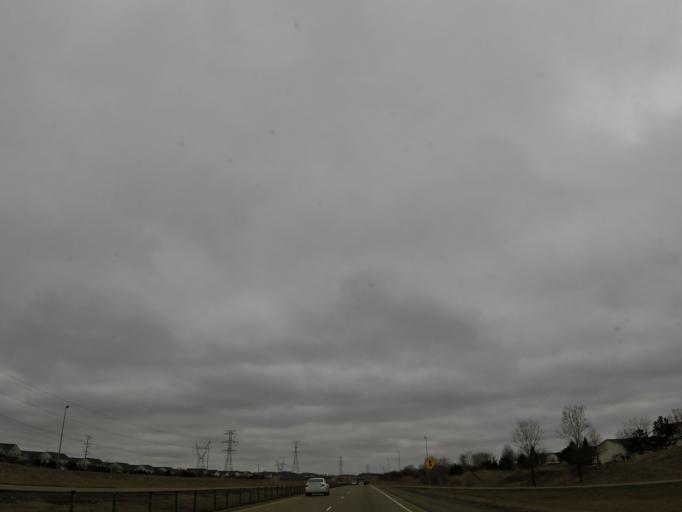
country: US
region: Minnesota
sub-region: Scott County
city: Shakopee
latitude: 44.7777
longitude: -93.5091
